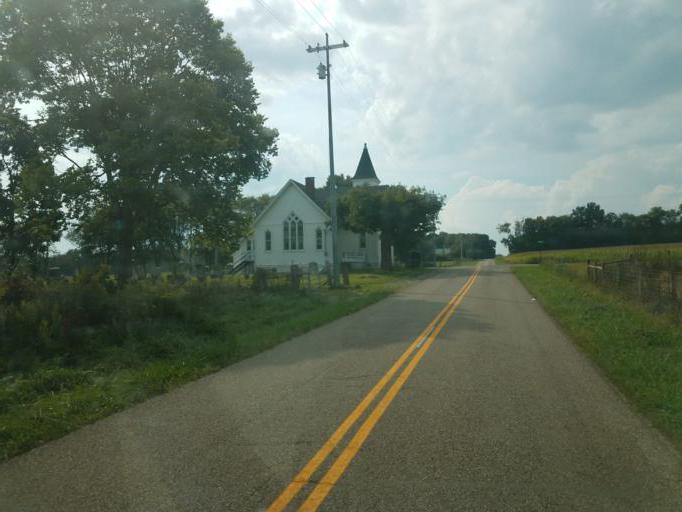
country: US
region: Ohio
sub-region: Knox County
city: Gambier
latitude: 40.3361
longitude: -82.3880
